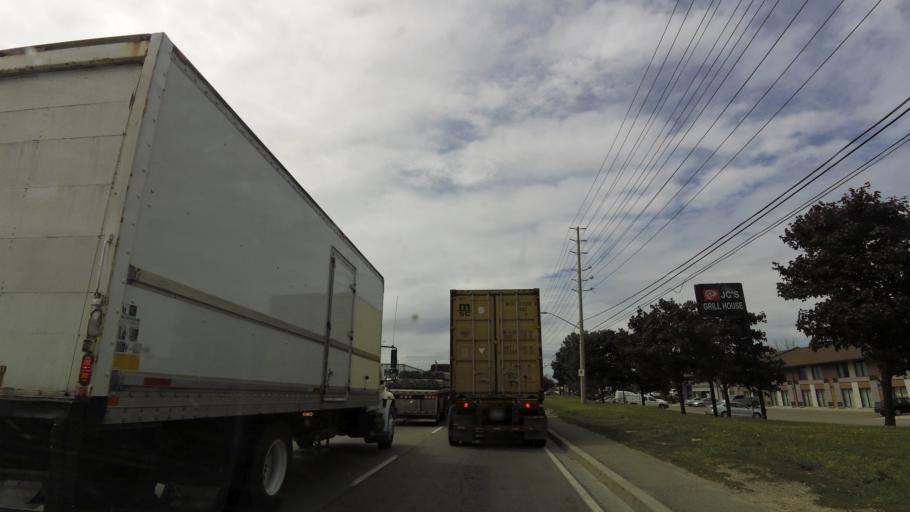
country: CA
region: Ontario
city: Etobicoke
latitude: 43.6418
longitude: -79.6289
